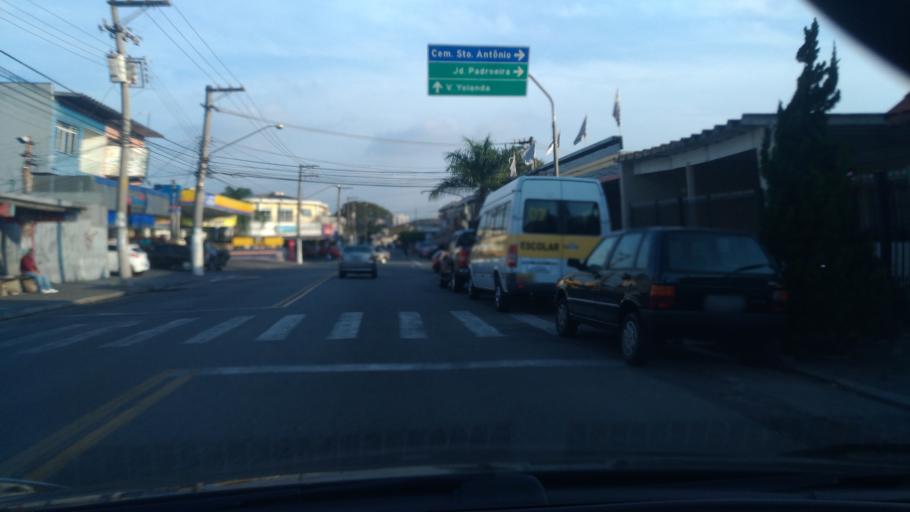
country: BR
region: Sao Paulo
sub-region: Osasco
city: Osasco
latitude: -23.5403
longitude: -46.7949
